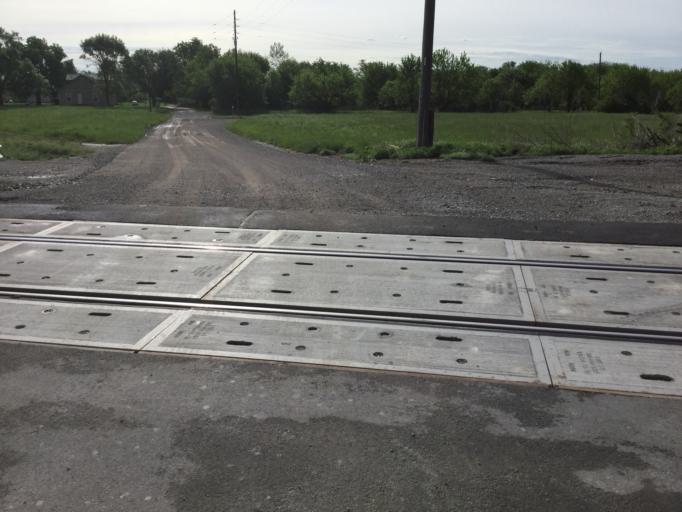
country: US
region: Kansas
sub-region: Linn County
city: Pleasanton
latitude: 38.0414
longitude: -94.6964
